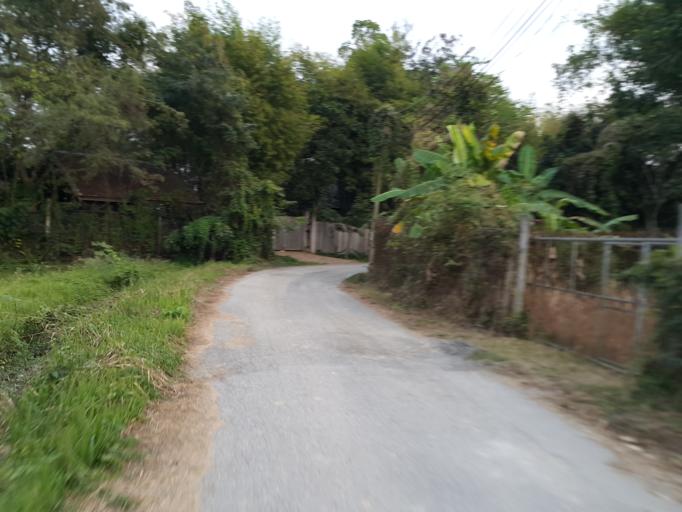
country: TH
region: Chiang Mai
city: San Sai
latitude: 18.8358
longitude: 99.1074
